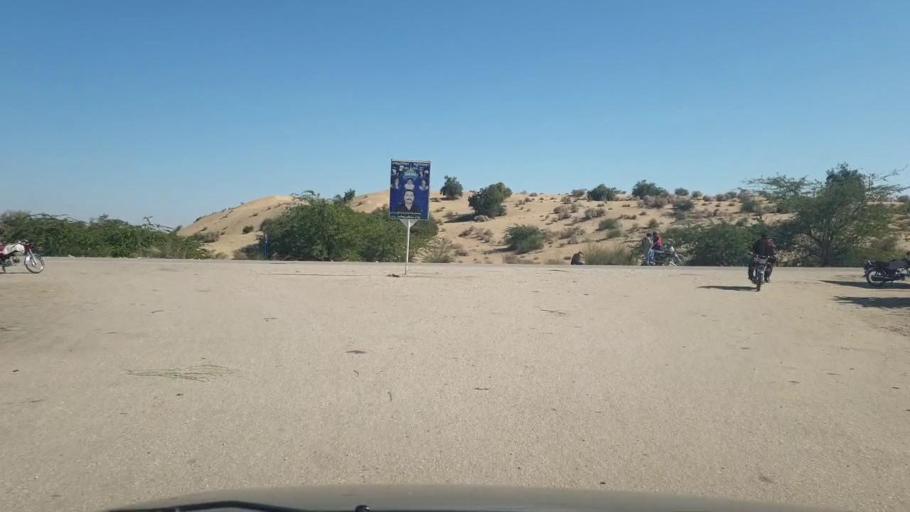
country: PK
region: Sindh
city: Bozdar
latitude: 27.0059
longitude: 68.9087
